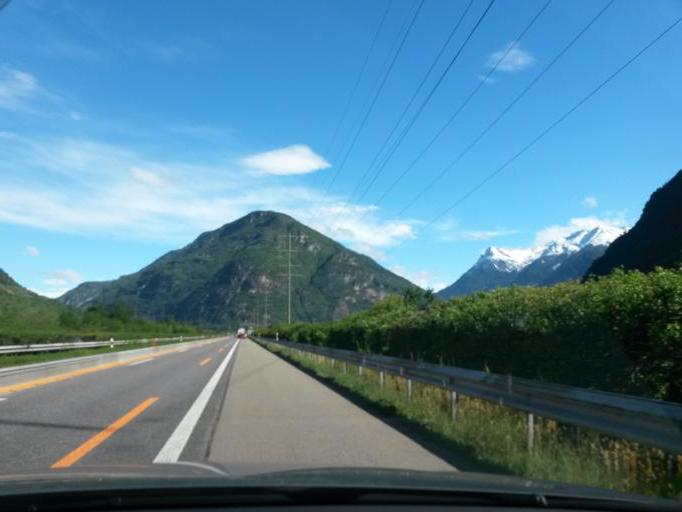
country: CH
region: Ticino
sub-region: Riviera District
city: Biasca
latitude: 46.3363
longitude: 8.9731
